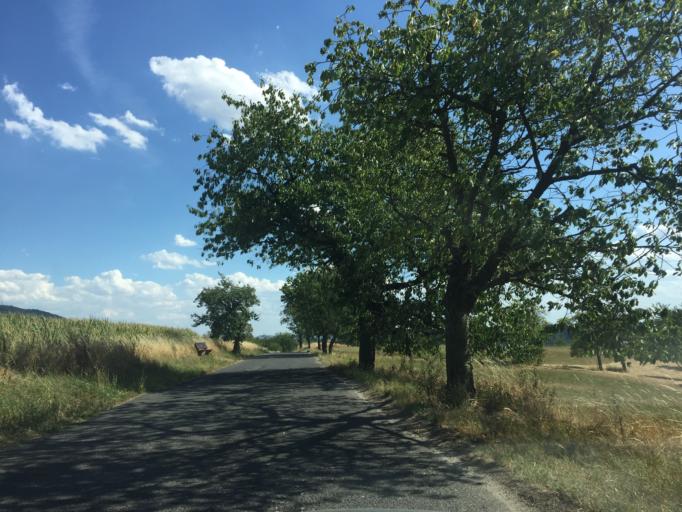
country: CZ
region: Liberecky
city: Mala Skala
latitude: 50.6252
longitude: 15.2141
